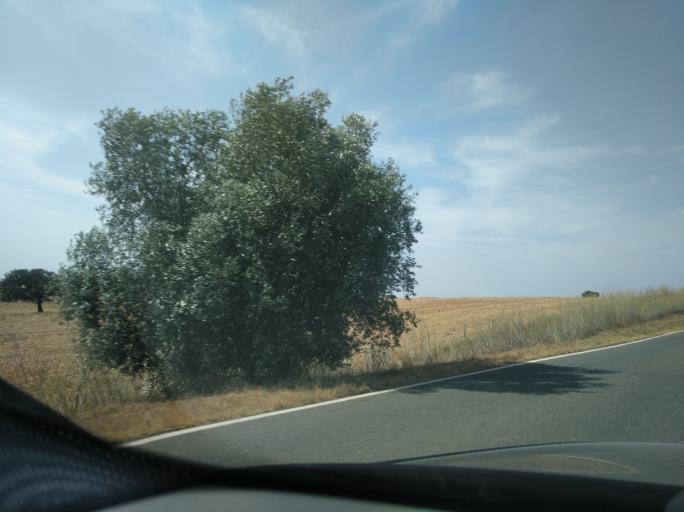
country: PT
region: Beja
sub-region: Beja
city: Beja
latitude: 37.8532
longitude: -7.8579
